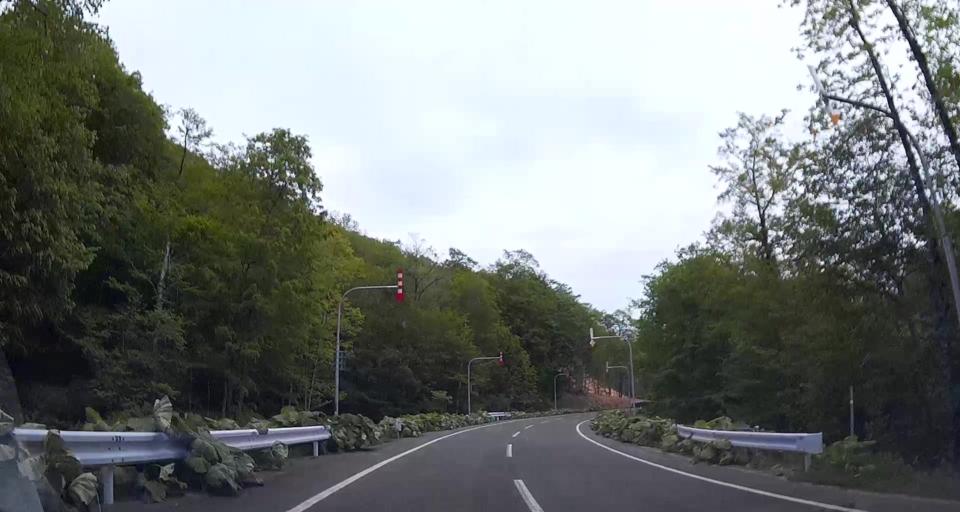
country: JP
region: Hokkaido
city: Chitose
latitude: 42.7926
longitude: 142.0559
